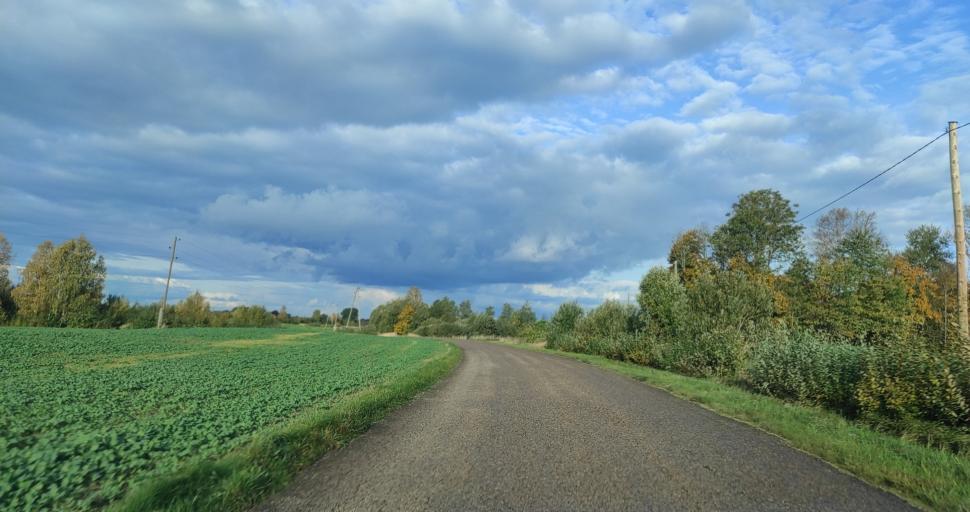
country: LV
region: Aizpute
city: Aizpute
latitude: 56.7795
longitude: 21.7749
